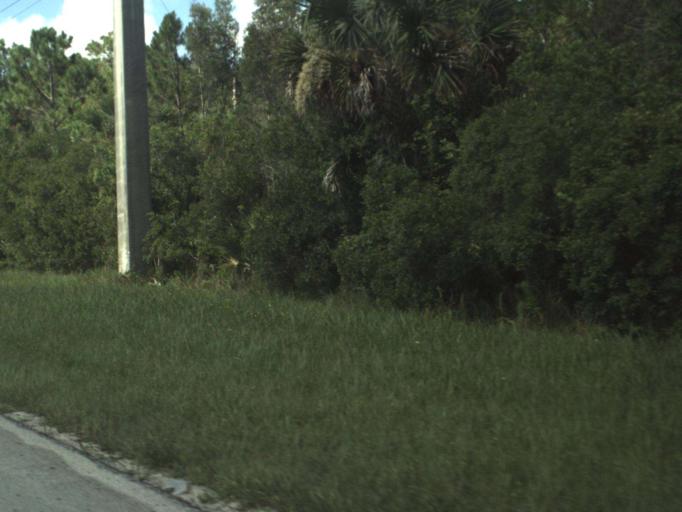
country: US
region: Florida
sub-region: Indian River County
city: Gifford
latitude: 27.6796
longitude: -80.4463
